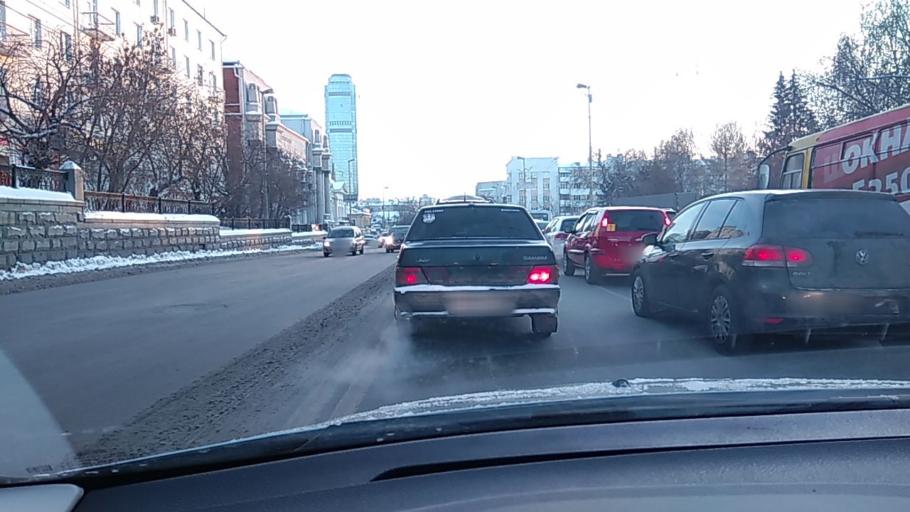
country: RU
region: Sverdlovsk
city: Yekaterinburg
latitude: 56.8436
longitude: 60.6099
